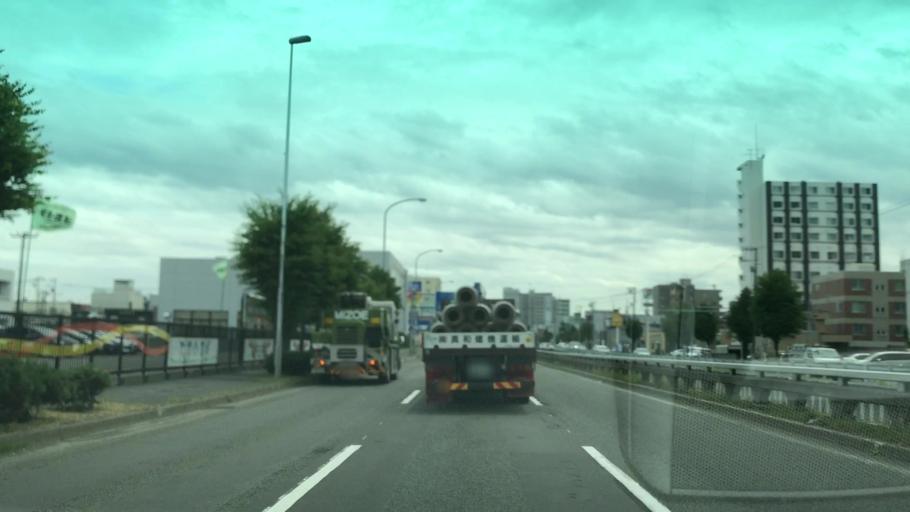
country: JP
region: Hokkaido
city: Sapporo
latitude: 43.0924
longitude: 141.3474
